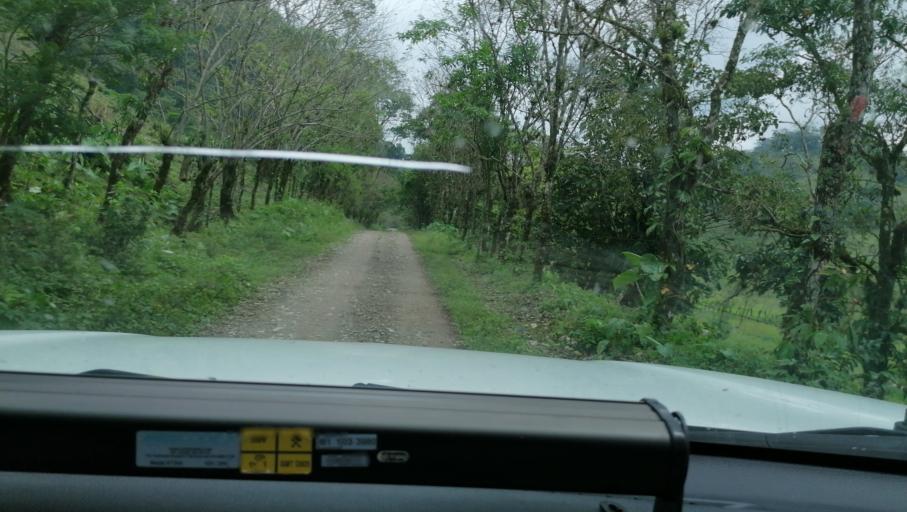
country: MX
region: Chiapas
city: Ixtacomitan
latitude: 17.3520
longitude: -93.1513
